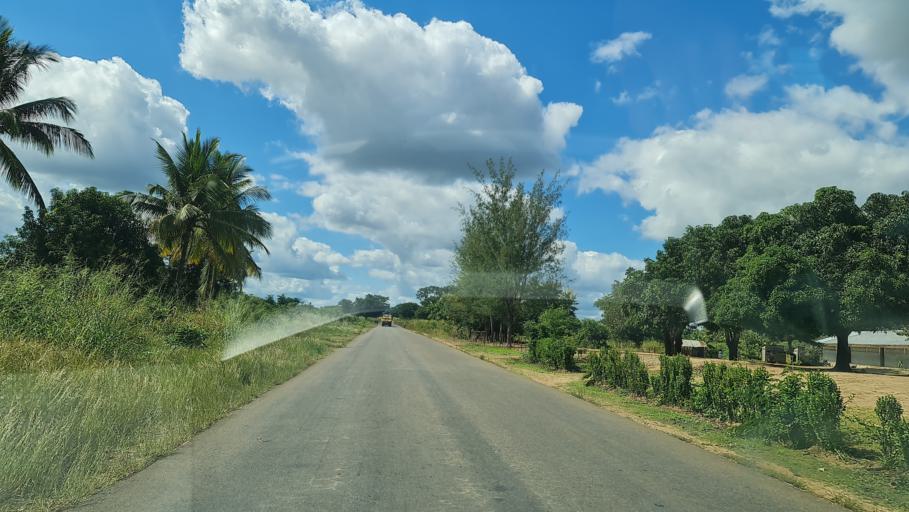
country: MZ
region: Zambezia
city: Quelimane
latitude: -17.5145
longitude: 36.2228
